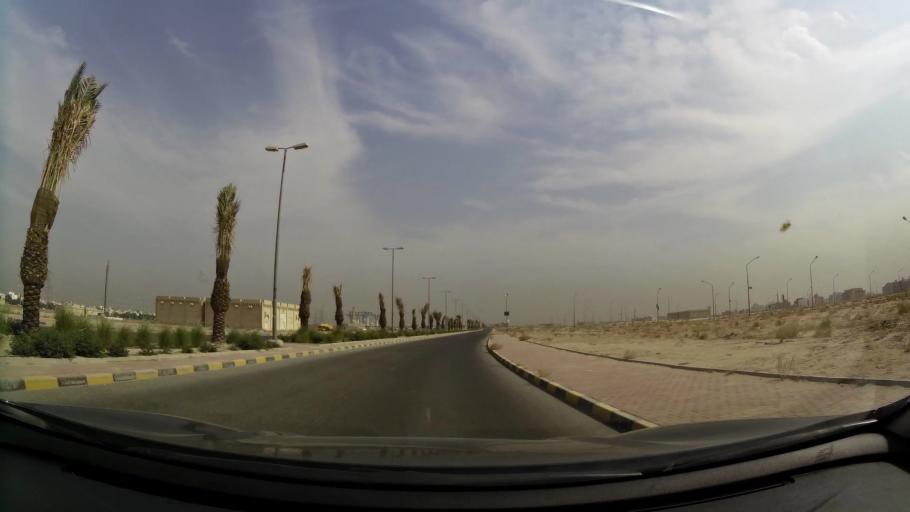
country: KW
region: Al Farwaniyah
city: Janub as Surrah
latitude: 29.2991
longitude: 47.9850
